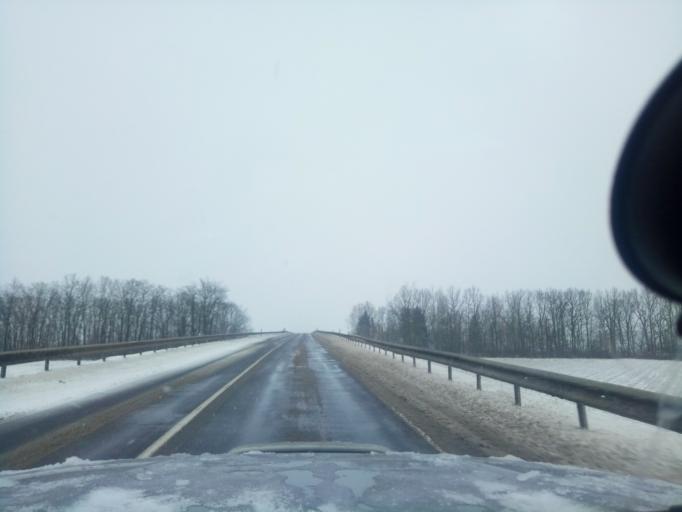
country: BY
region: Minsk
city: Haradzyeya
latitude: 53.3310
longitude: 26.5467
